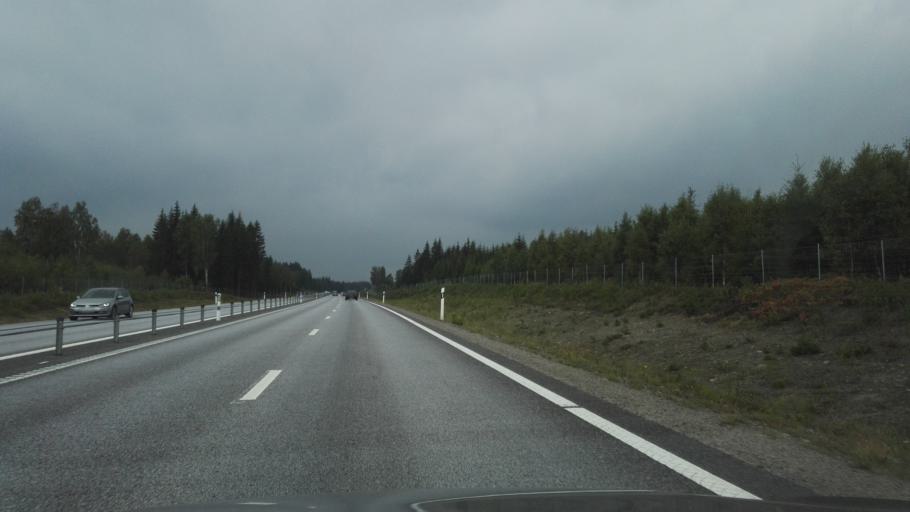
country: SE
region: Kronoberg
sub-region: Vaxjo Kommun
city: Gemla
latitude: 56.9068
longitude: 14.6539
